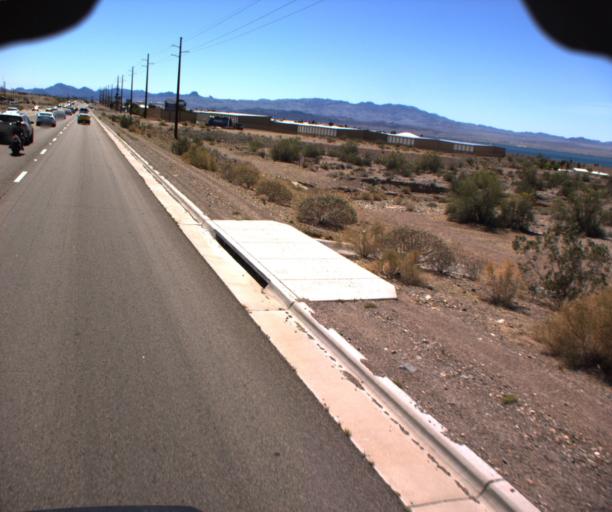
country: US
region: Arizona
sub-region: Mohave County
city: Desert Hills
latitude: 34.5428
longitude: -114.3540
